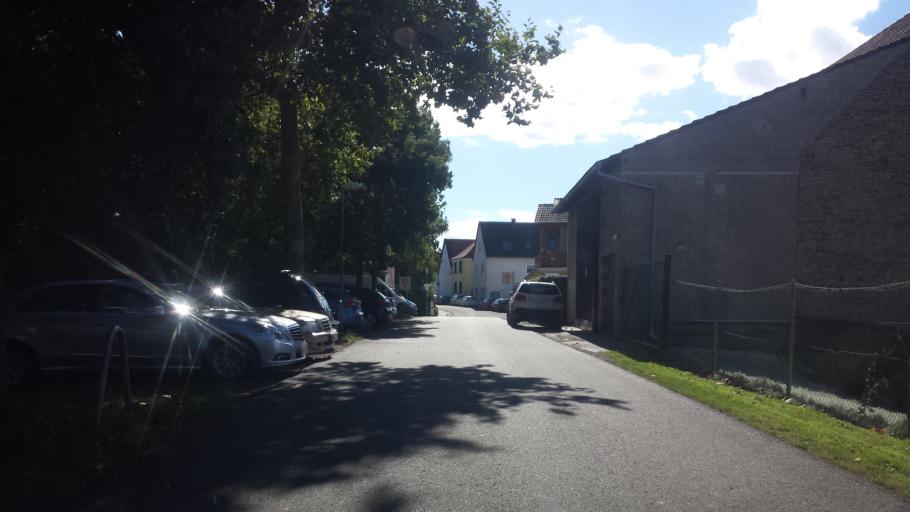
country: DE
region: Rheinland-Pfalz
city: Bobenheim-Roxheim
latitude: 49.5794
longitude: 8.3689
